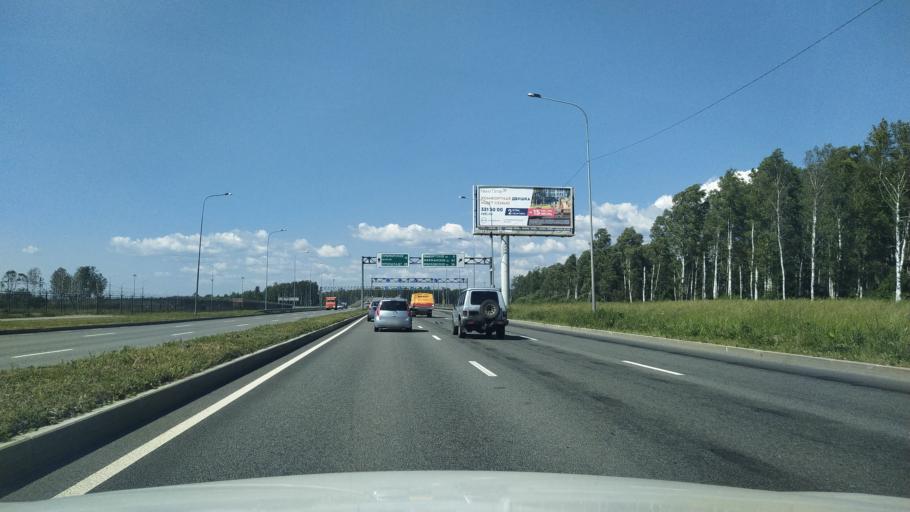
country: RU
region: St.-Petersburg
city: Levashovo
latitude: 60.0710
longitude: 30.1851
